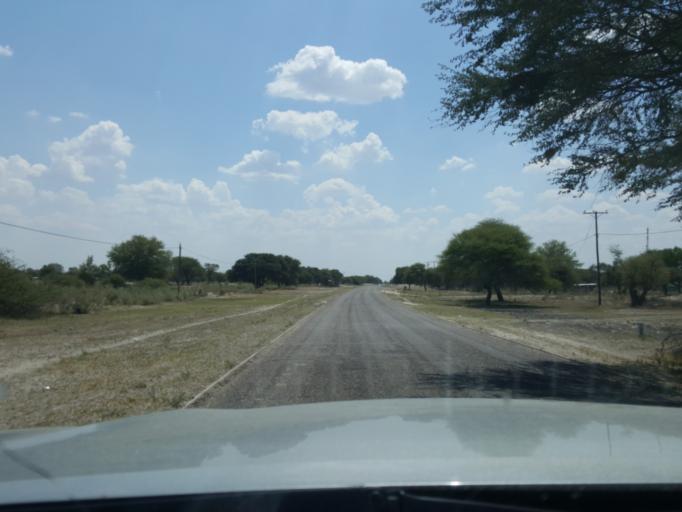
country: BW
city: Tsau
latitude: -20.1782
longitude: 22.4617
